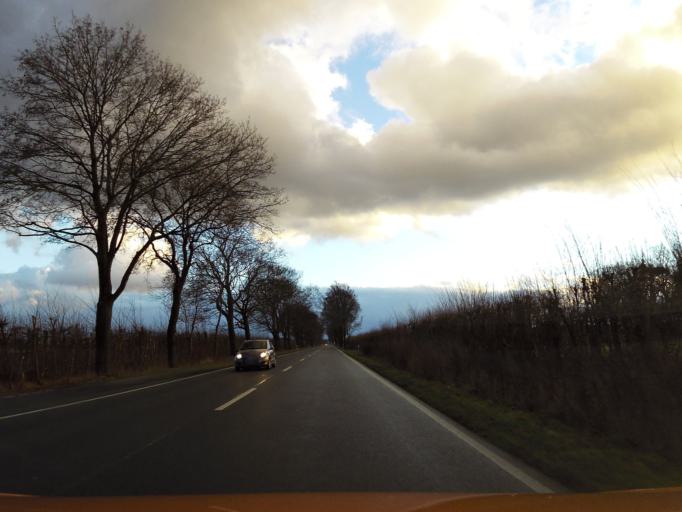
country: DE
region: Lower Saxony
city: Didderse
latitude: 52.3870
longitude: 10.3759
